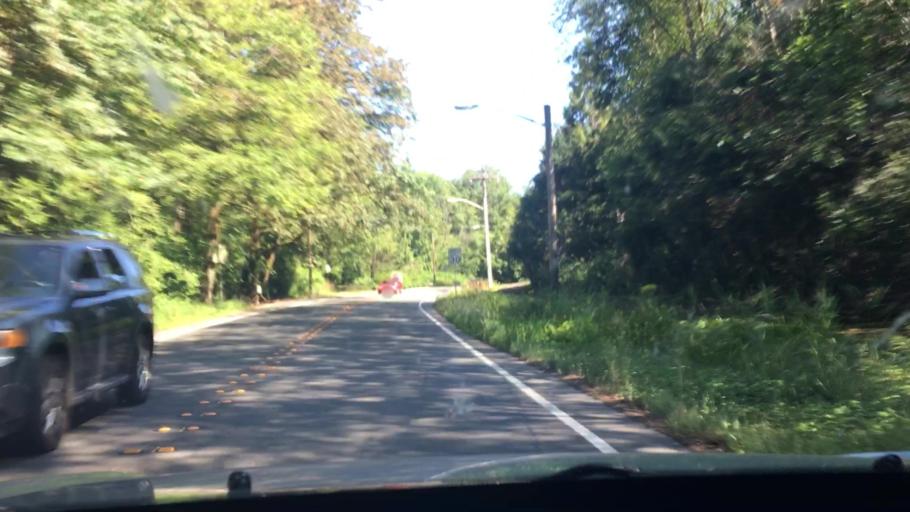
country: US
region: Washington
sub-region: King County
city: Newcastle
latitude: 47.5425
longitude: -122.1302
